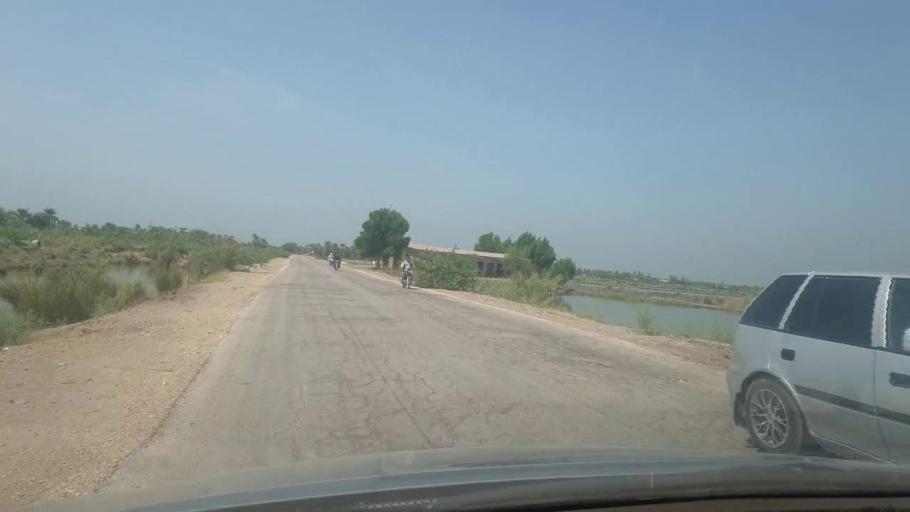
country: PK
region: Sindh
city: Ranipur
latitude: 27.2520
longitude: 68.5838
